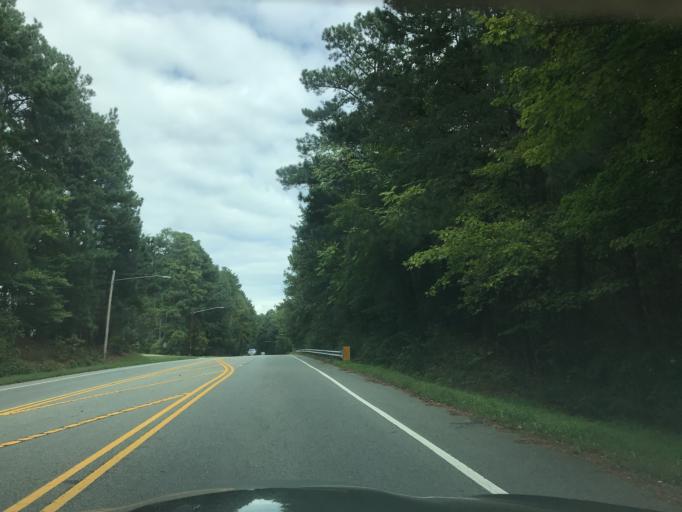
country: US
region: North Carolina
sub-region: Orange County
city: Chapel Hill
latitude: 35.9298
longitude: -79.0659
